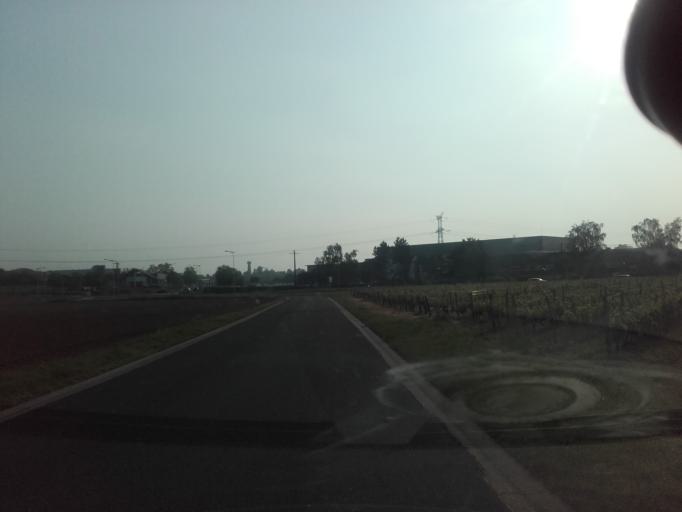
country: FR
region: Centre
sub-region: Departement d'Indre-et-Loire
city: Vouvray
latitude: 47.4314
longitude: 0.7954
